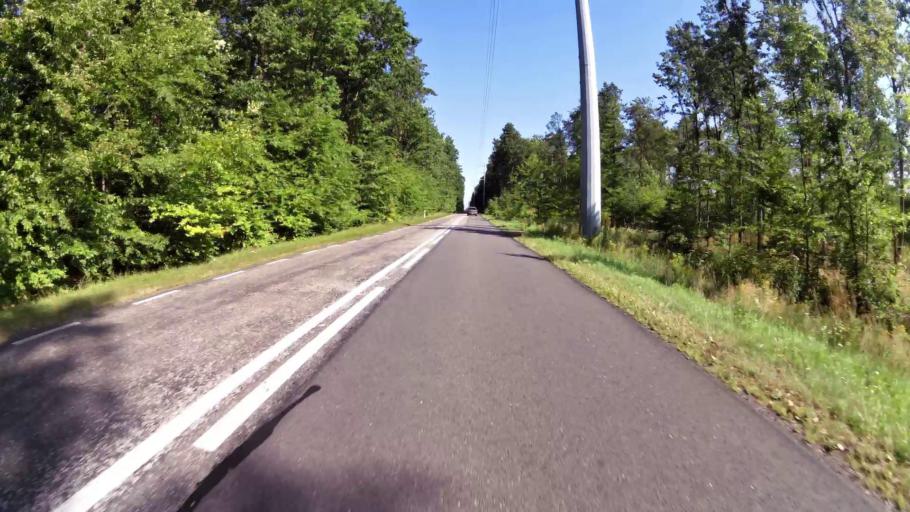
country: PL
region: West Pomeranian Voivodeship
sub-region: Powiat drawski
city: Czaplinek
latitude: 53.4483
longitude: 16.2127
